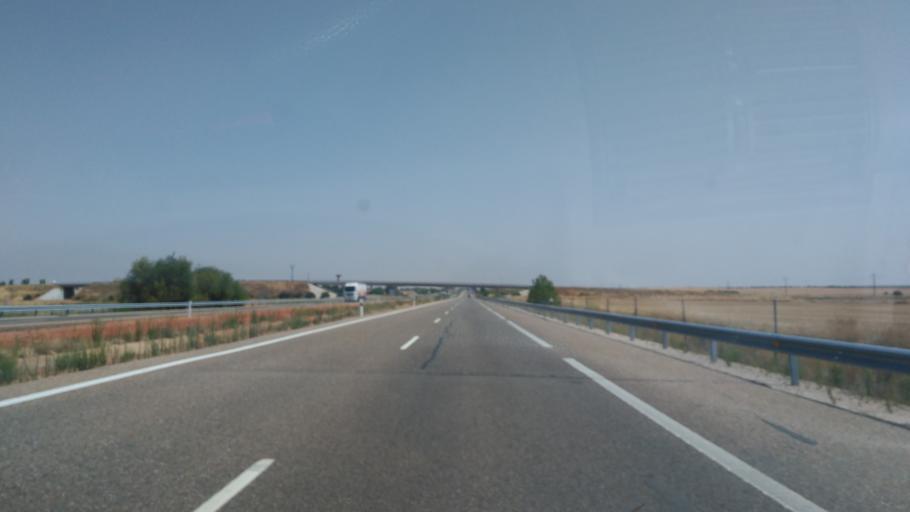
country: ES
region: Castille and Leon
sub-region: Provincia de Salamanca
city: Calzada de Don Diego
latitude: 40.8988
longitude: -5.9122
